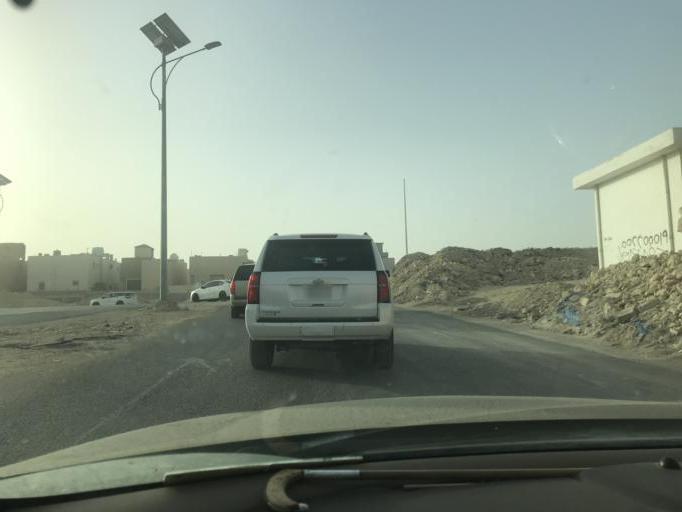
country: SA
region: Ar Riyad
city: Riyadh
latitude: 24.8387
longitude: 46.6676
